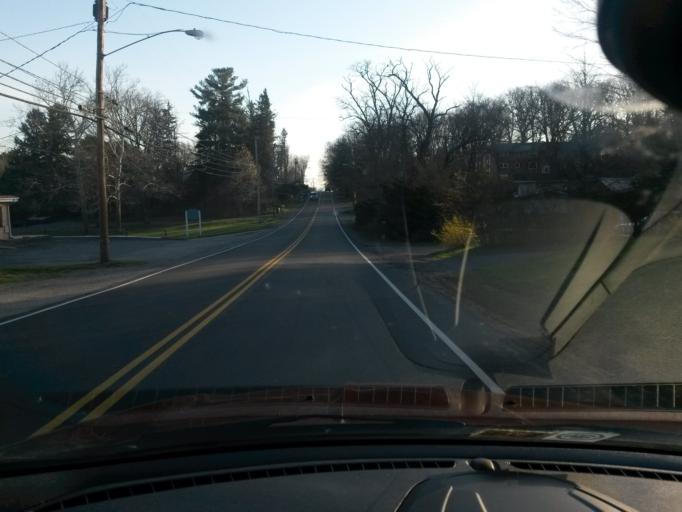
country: US
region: Virginia
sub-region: Montgomery County
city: Christiansburg
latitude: 37.1203
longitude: -80.4194
